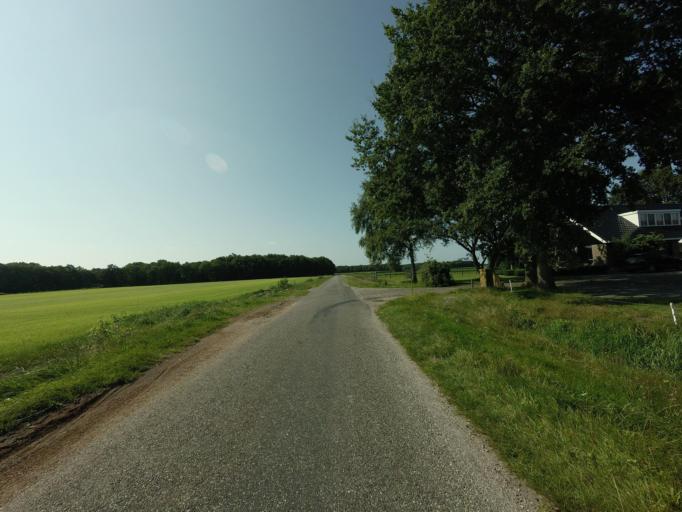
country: NL
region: Drenthe
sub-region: Gemeente Tynaarlo
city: Vries
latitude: 53.0877
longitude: 6.5745
